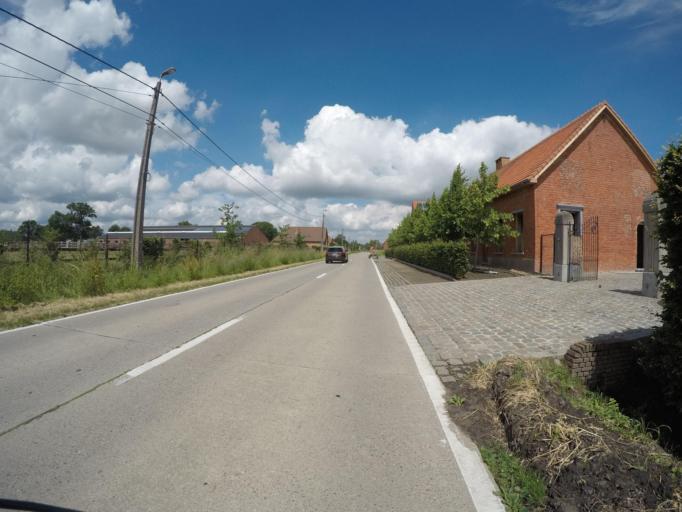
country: BE
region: Flanders
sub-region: Provincie Antwerpen
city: Brecht
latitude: 51.3597
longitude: 4.6898
